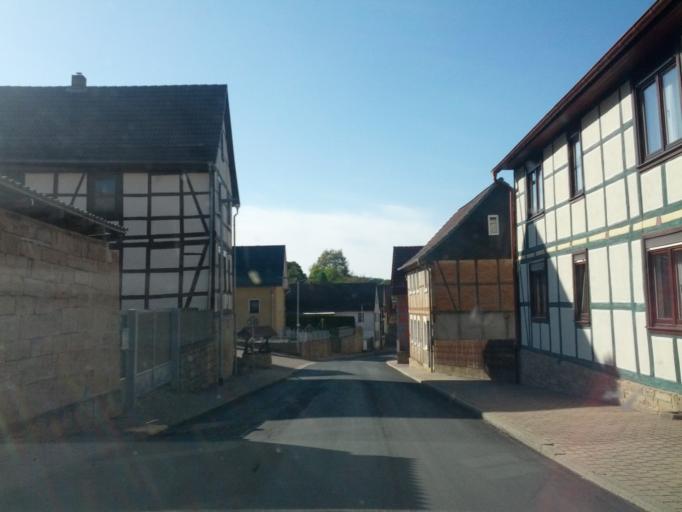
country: DE
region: Hesse
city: Wanfried
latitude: 51.2015
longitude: 10.2134
